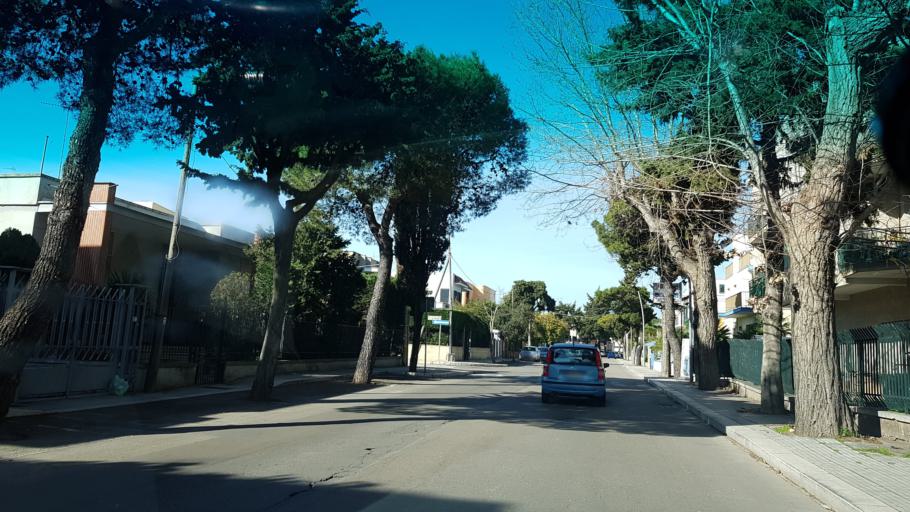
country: IT
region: Apulia
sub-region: Provincia di Lecce
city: Lecce
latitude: 40.3449
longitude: 18.1563
